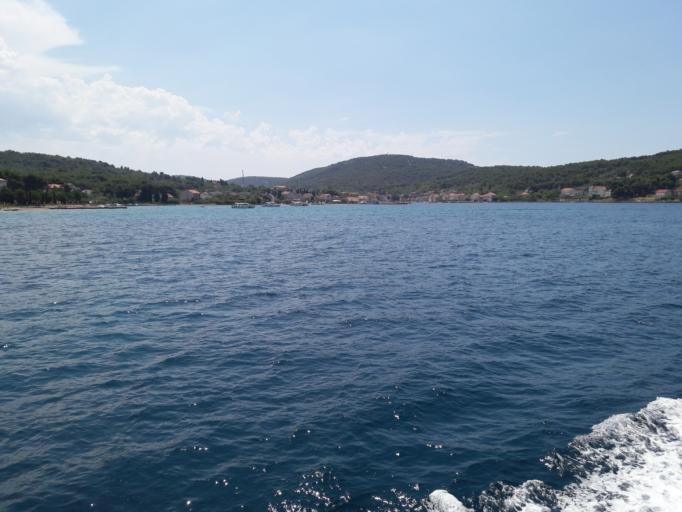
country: HR
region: Sibensko-Kniniska
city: Vodice
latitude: 43.7049
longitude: 15.8300
